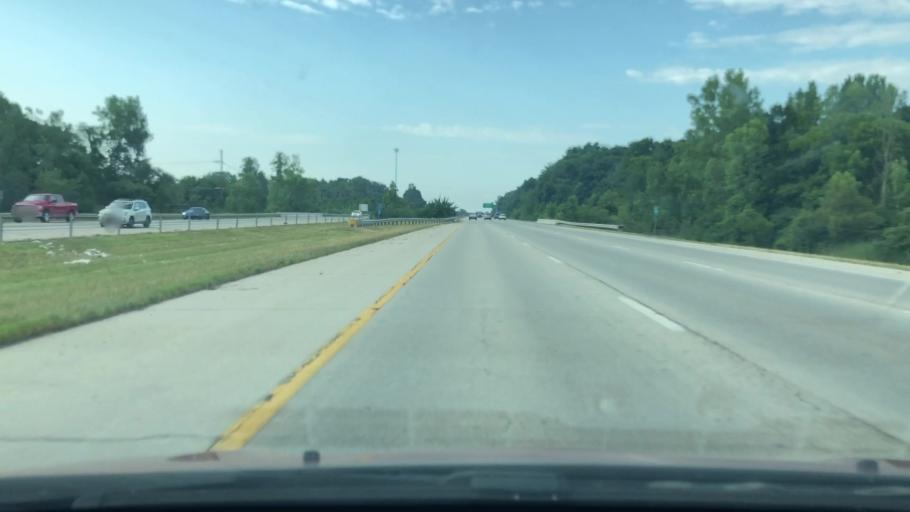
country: US
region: Ohio
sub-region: Greene County
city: Bellbrook
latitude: 39.6747
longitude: -84.0999
